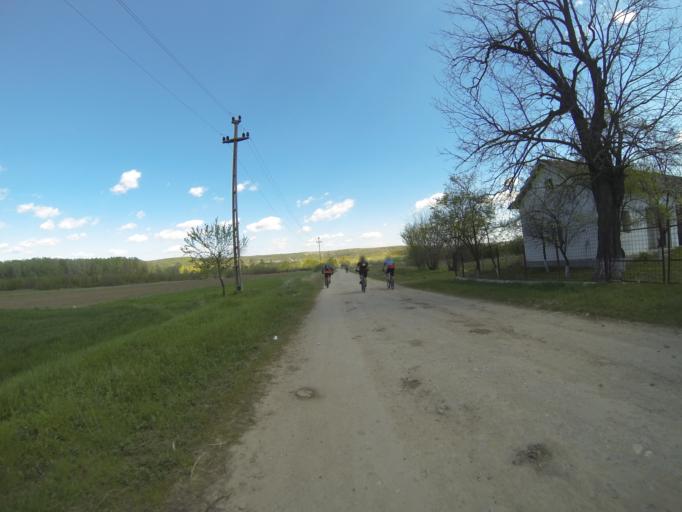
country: RO
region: Dolj
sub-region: Comuna Goesti
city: Goesti
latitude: 44.4990
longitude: 23.7372
